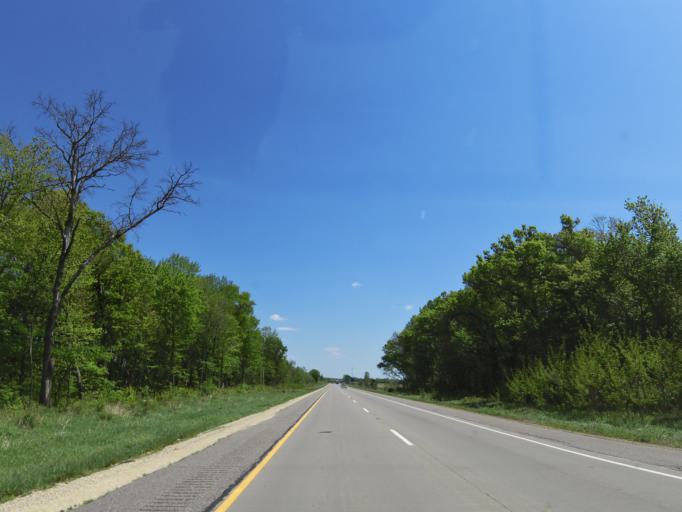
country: US
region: Wisconsin
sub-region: Juneau County
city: New Lisbon
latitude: 43.8978
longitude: -90.1844
